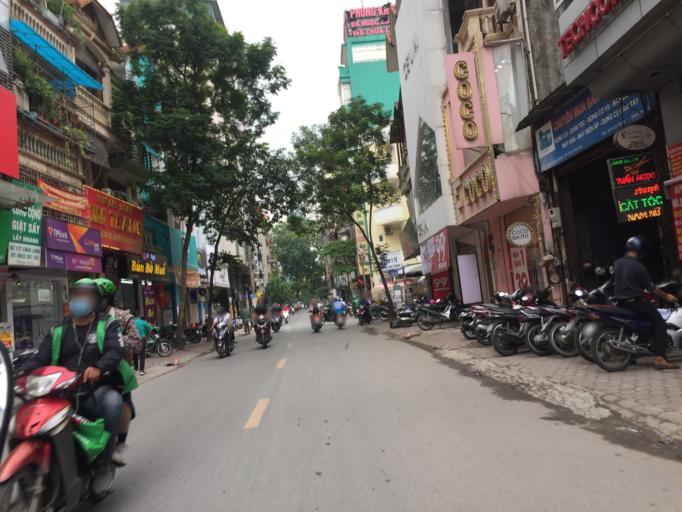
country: VN
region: Ha Noi
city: Cau Giay
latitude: 21.0231
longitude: 105.8017
